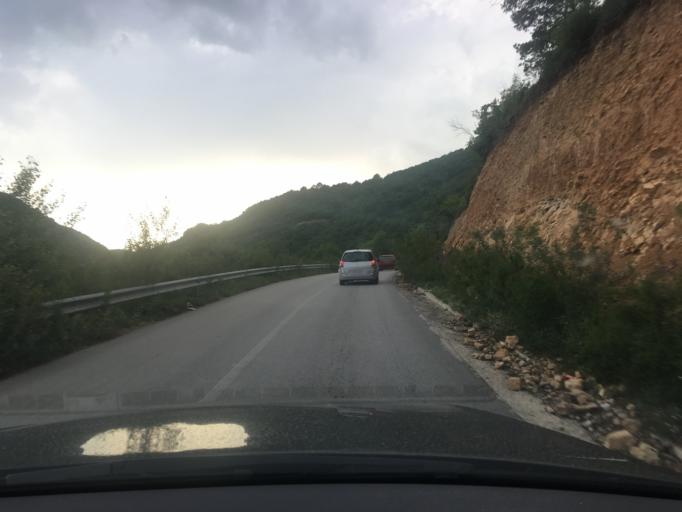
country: XK
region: Ferizaj
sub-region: Hani i Elezit
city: Hani i Elezit
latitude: 42.1455
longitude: 21.2764
